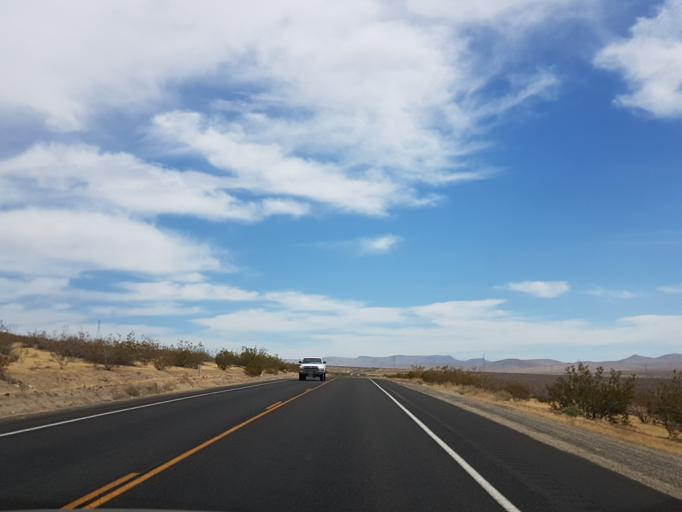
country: US
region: California
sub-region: Kern County
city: Ridgecrest
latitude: 35.4266
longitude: -117.7161
